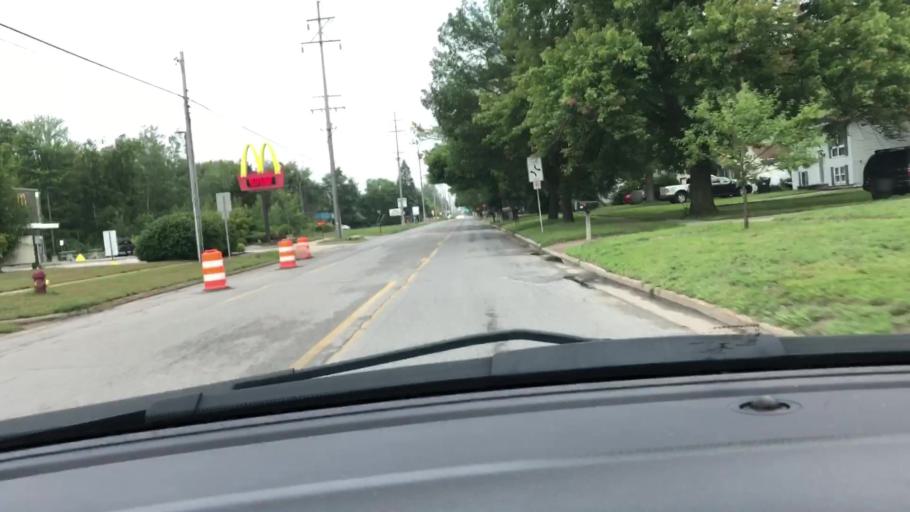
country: US
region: Michigan
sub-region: Midland County
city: Midland
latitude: 43.6054
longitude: -84.1875
